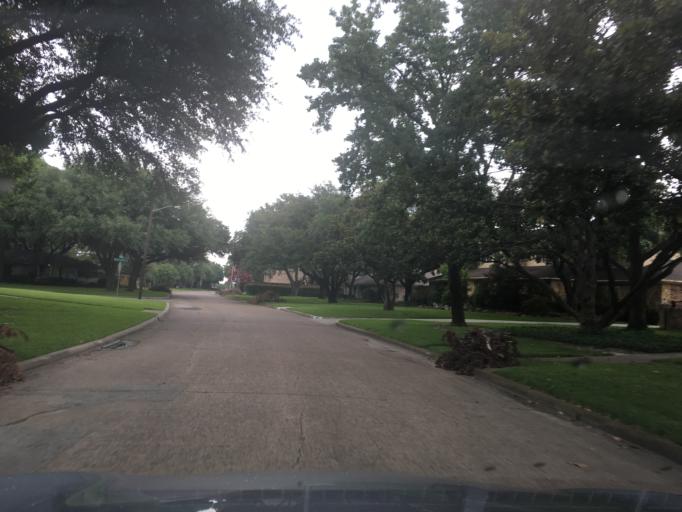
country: US
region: Texas
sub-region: Dallas County
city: Addison
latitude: 32.9107
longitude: -96.8090
